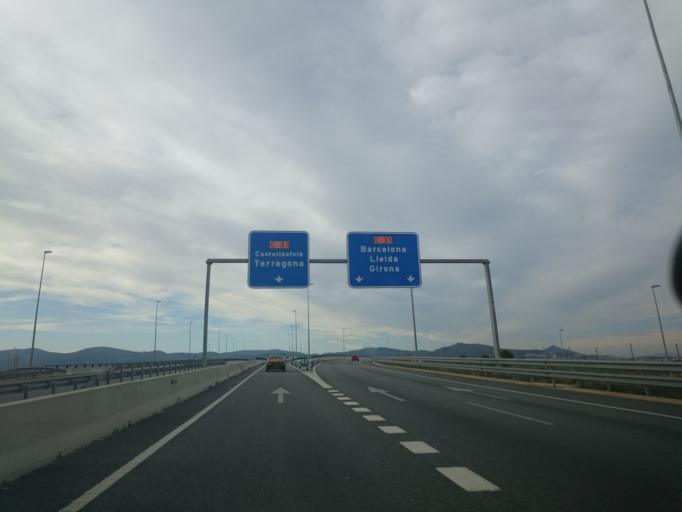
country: ES
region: Catalonia
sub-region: Provincia de Barcelona
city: Viladecans
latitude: 41.2943
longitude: 2.0535
